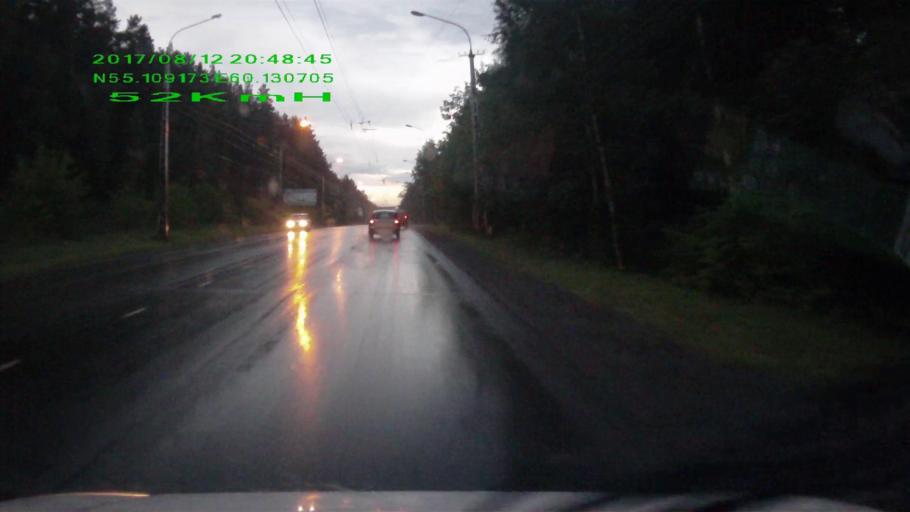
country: RU
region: Chelyabinsk
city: Turgoyak
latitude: 55.1094
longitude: 60.1307
